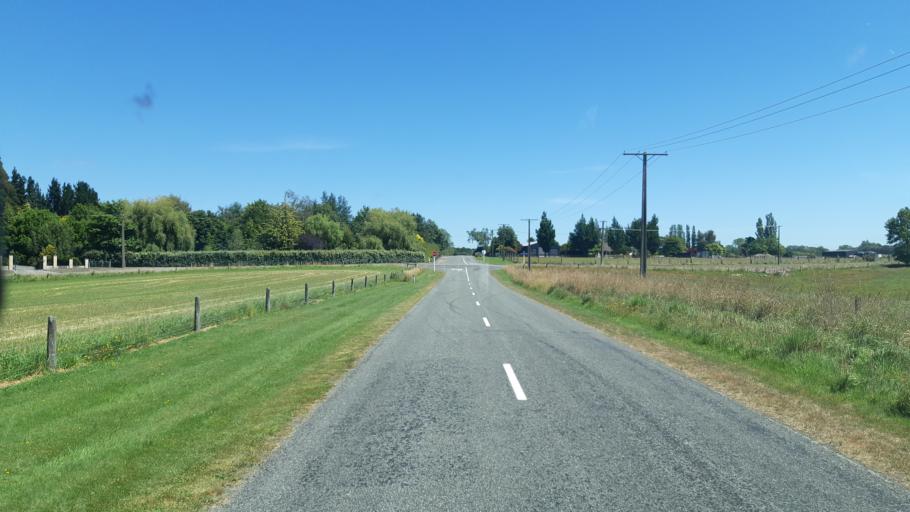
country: NZ
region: Canterbury
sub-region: Timaru District
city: Timaru
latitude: -44.3929
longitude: 171.1415
